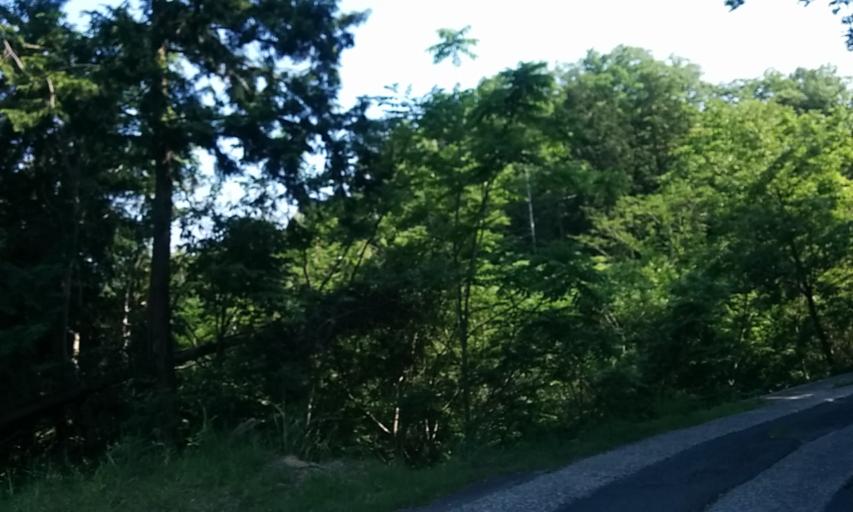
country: JP
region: Kyoto
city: Miyazu
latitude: 35.5878
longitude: 135.1920
